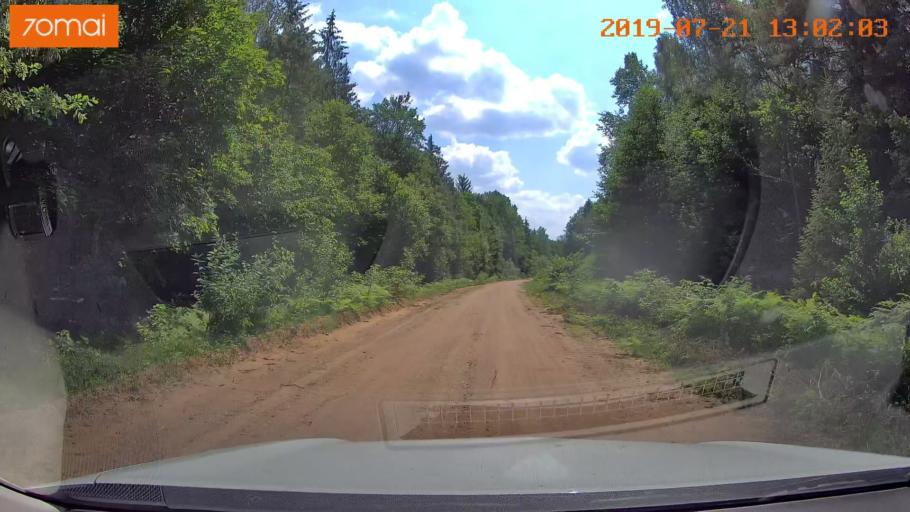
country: BY
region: Grodnenskaya
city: Lyubcha
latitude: 53.8495
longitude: 26.0235
